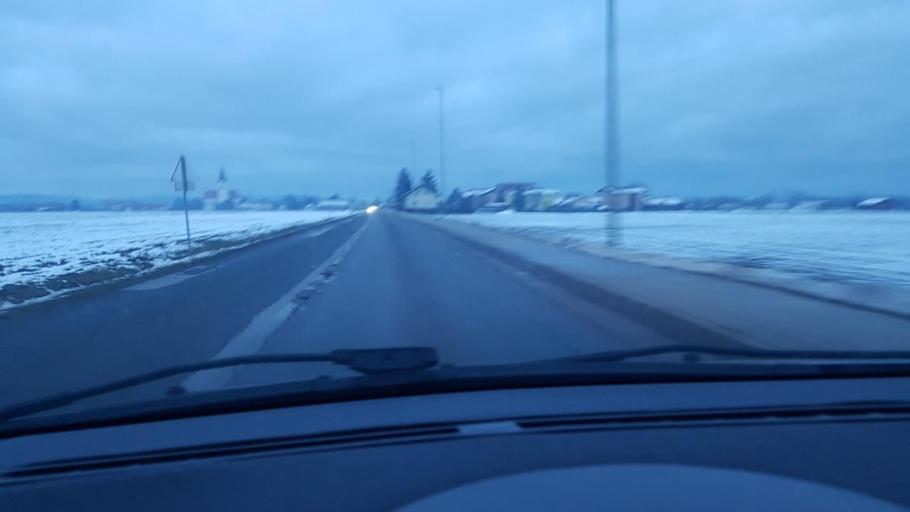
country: SI
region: Hajdina
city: Spodnja Hajdina
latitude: 46.4016
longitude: 15.8317
